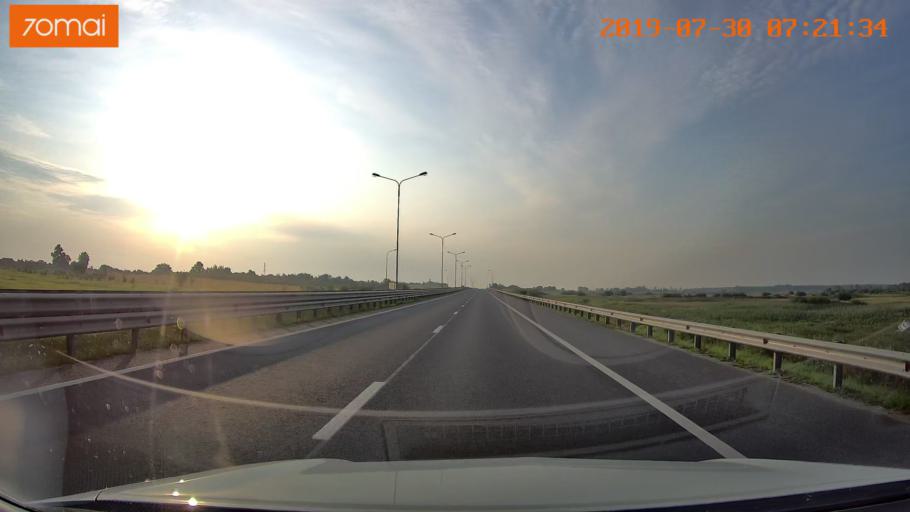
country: RU
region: Kaliningrad
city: Bol'shoe Isakovo
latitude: 54.6957
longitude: 20.7326
